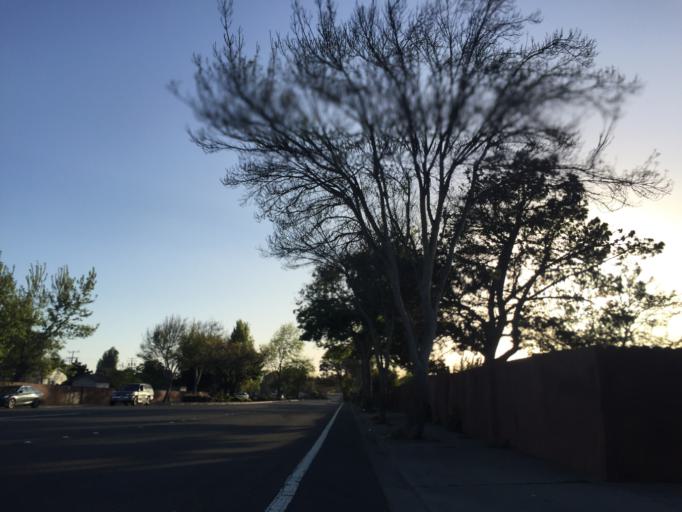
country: US
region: California
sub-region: Contra Costa County
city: San Pablo
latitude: 37.9665
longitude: -122.3513
